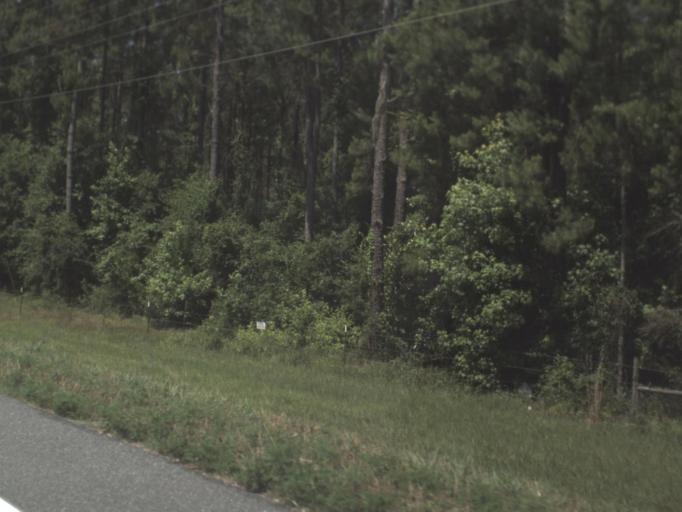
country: US
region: Florida
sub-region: Levy County
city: Williston
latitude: 29.4824
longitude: -82.4145
